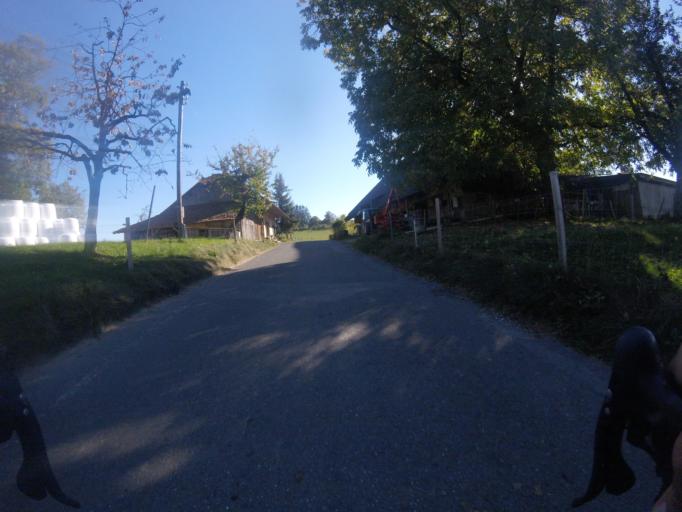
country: CH
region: Bern
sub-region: Seeland District
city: Schupfen
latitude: 47.0268
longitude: 7.3939
